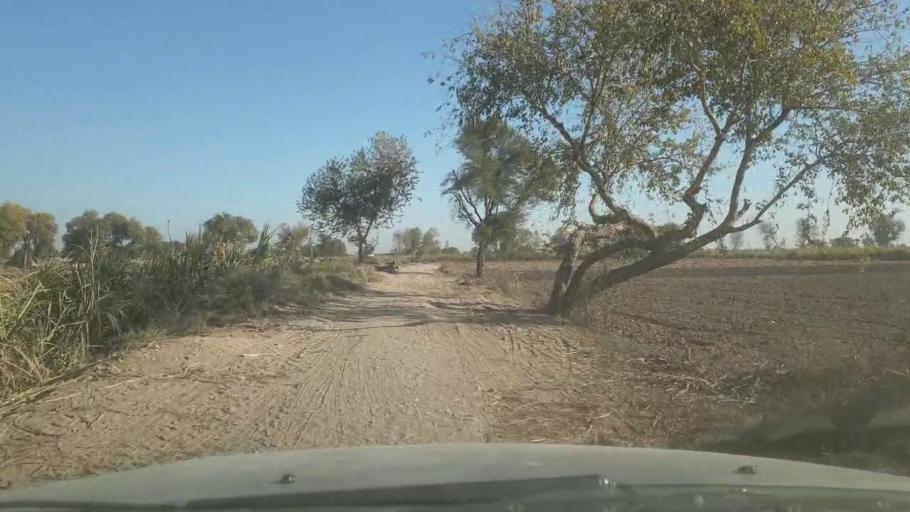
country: PK
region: Sindh
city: Adilpur
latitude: 27.9617
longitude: 69.2039
